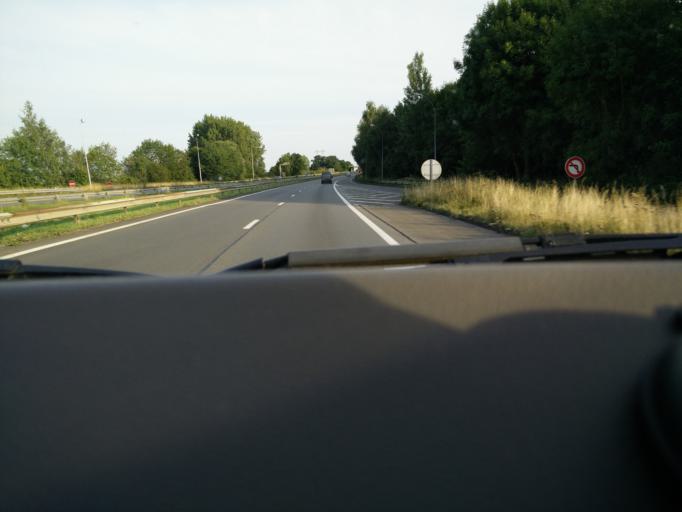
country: FR
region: Nord-Pas-de-Calais
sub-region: Departement du Nord
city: Genech
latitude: 50.5168
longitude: 3.2076
